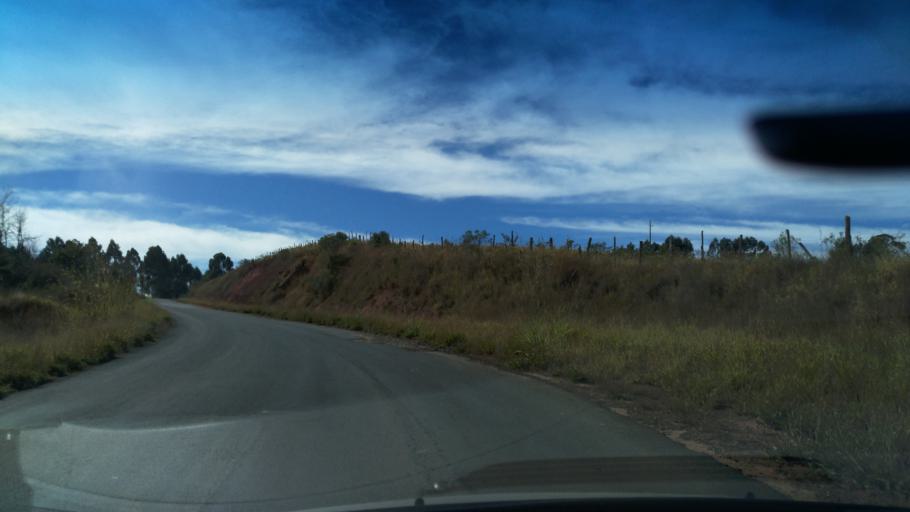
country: BR
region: Minas Gerais
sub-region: Andradas
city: Andradas
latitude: -22.0444
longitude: -46.3409
